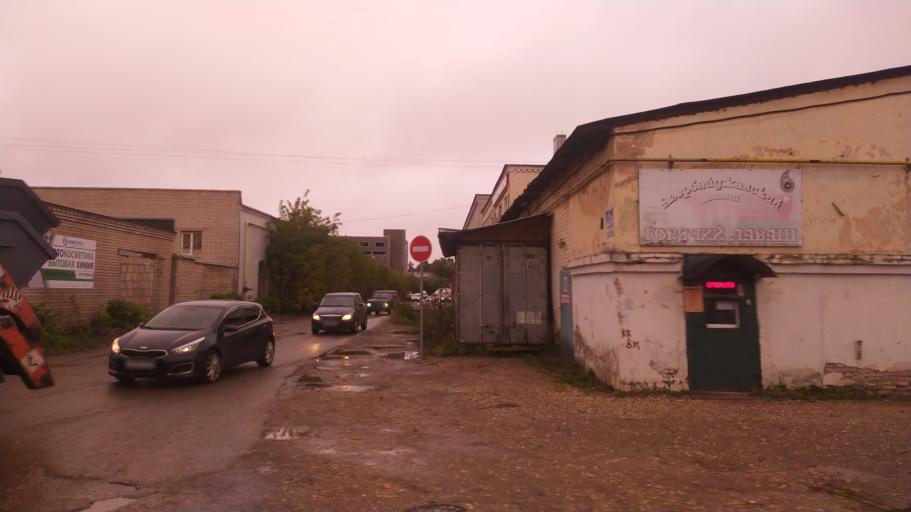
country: RU
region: Tverskaya
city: Tver
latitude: 56.8300
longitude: 35.9110
